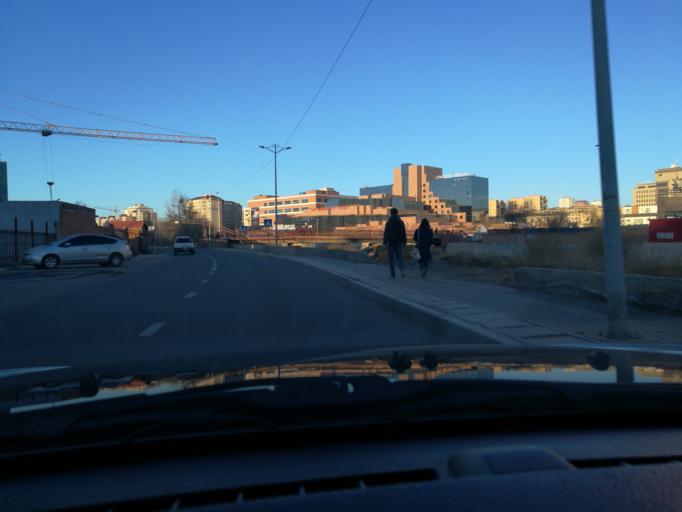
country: MN
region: Ulaanbaatar
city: Ulaanbaatar
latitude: 47.9201
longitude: 106.9306
